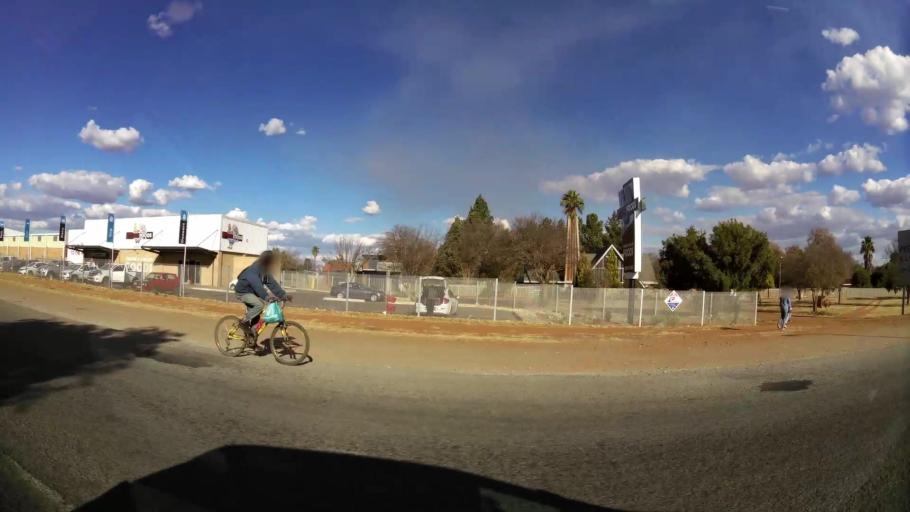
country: ZA
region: North-West
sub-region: Dr Kenneth Kaunda District Municipality
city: Klerksdorp
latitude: -26.8575
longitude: 26.6744
